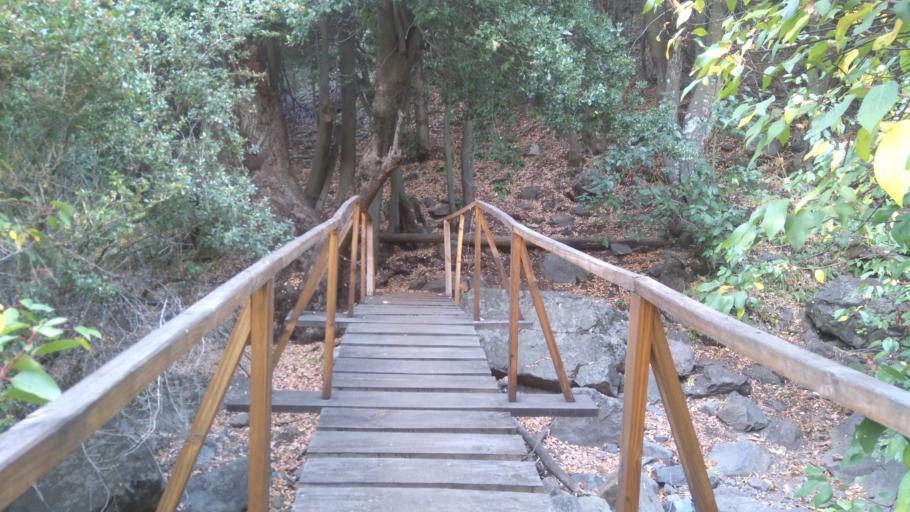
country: CL
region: Santiago Metropolitan
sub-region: Provincia de Cordillera
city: Puente Alto
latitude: -33.7104
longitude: -70.4475
